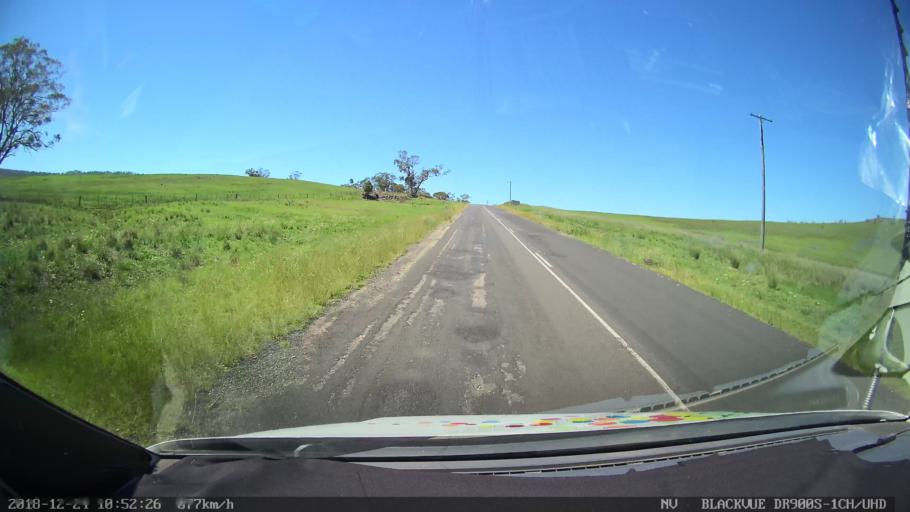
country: AU
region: New South Wales
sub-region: Upper Hunter Shire
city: Merriwa
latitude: -31.9805
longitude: 150.4221
